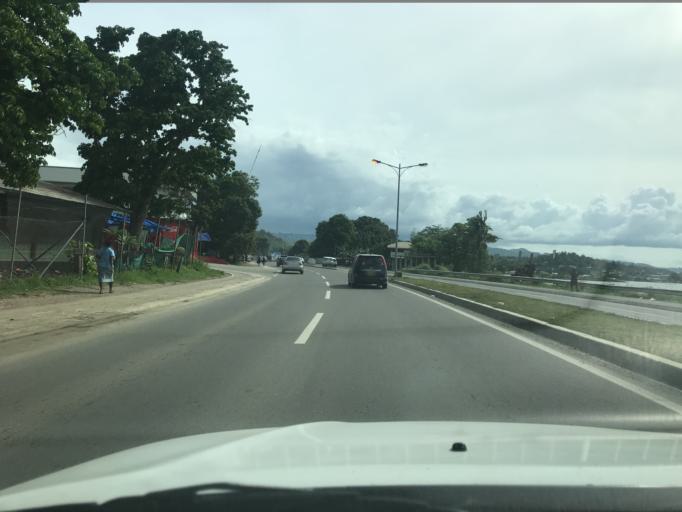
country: SB
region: Guadalcanal
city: Honiara
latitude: -9.4338
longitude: 159.9758
